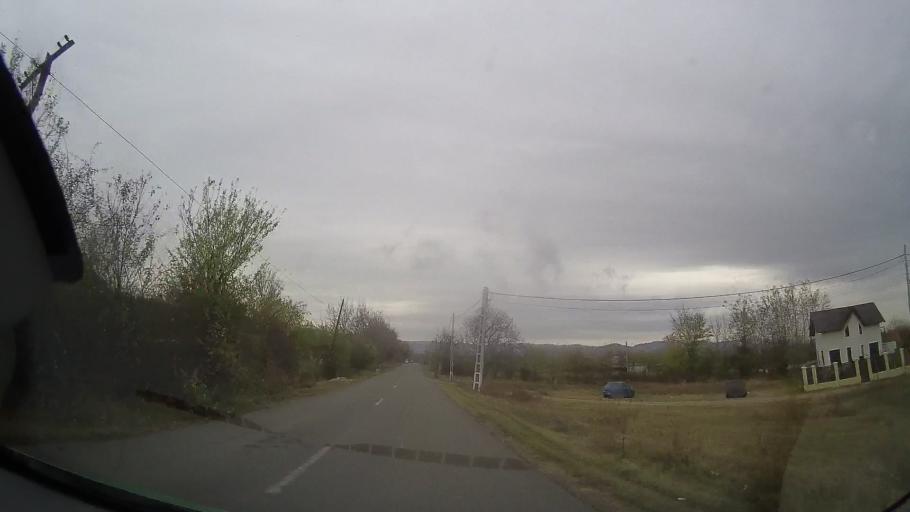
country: RO
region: Prahova
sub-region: Comuna Vadu Sapat
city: Vadu Sapat
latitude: 45.0282
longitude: 26.3838
